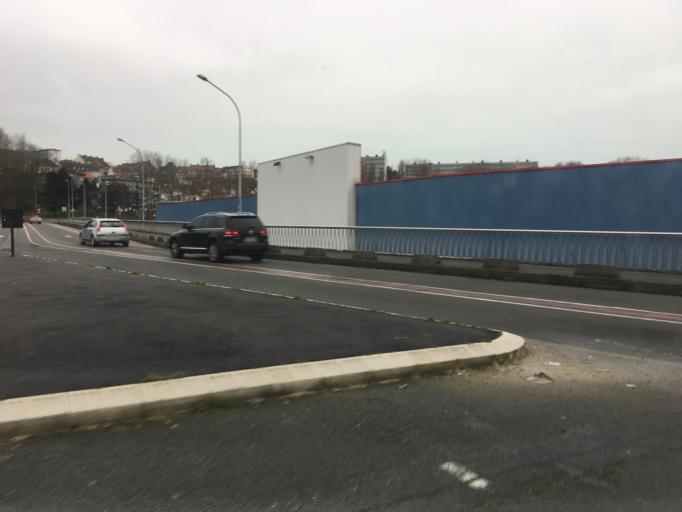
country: FR
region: Nord-Pas-de-Calais
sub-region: Departement du Pas-de-Calais
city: Outreau
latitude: 50.7182
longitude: 1.5969
